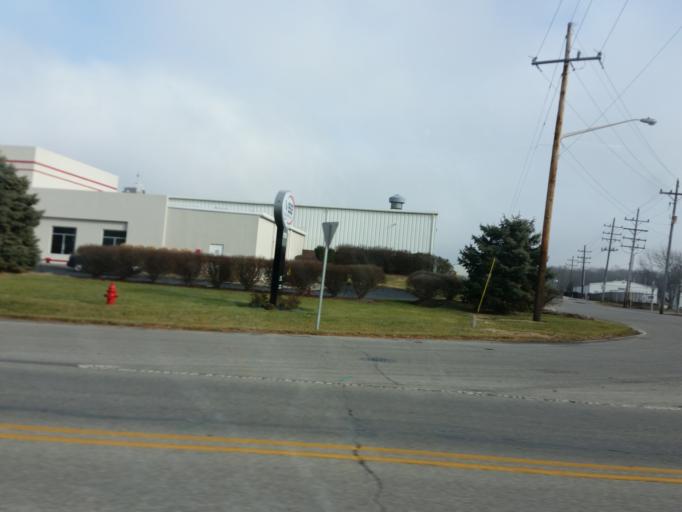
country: US
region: Indiana
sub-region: Jefferson County
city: North Madison
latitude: 38.7760
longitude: -85.4194
